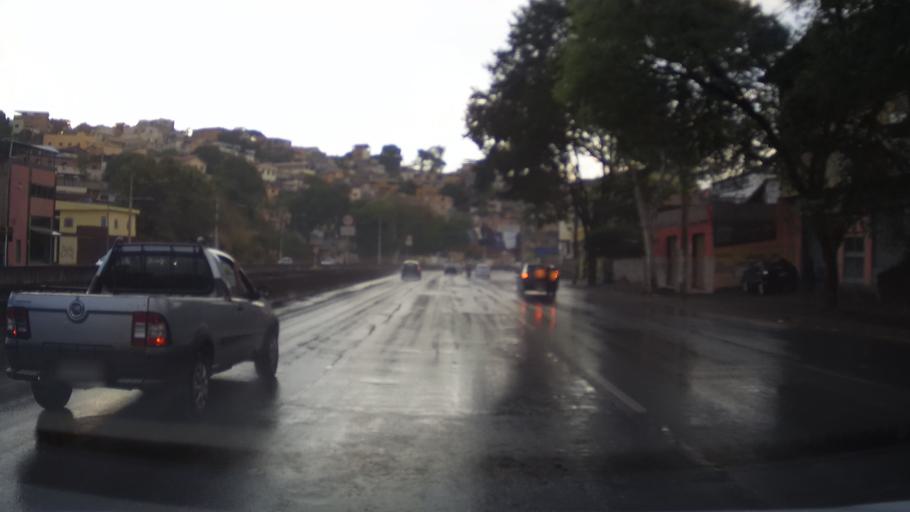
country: BR
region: Minas Gerais
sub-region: Belo Horizonte
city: Belo Horizonte
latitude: -19.9484
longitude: -43.9854
